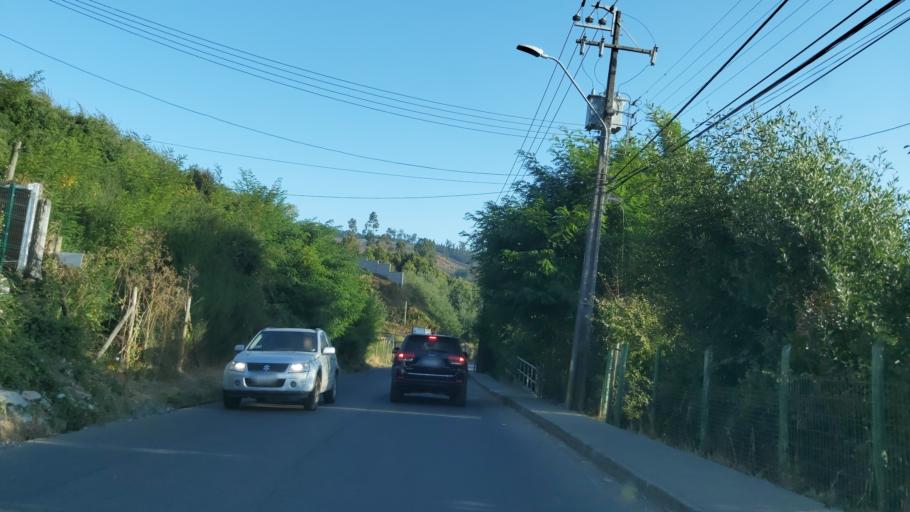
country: CL
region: Biobio
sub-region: Provincia de Concepcion
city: Tome
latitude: -36.5411
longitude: -72.9314
